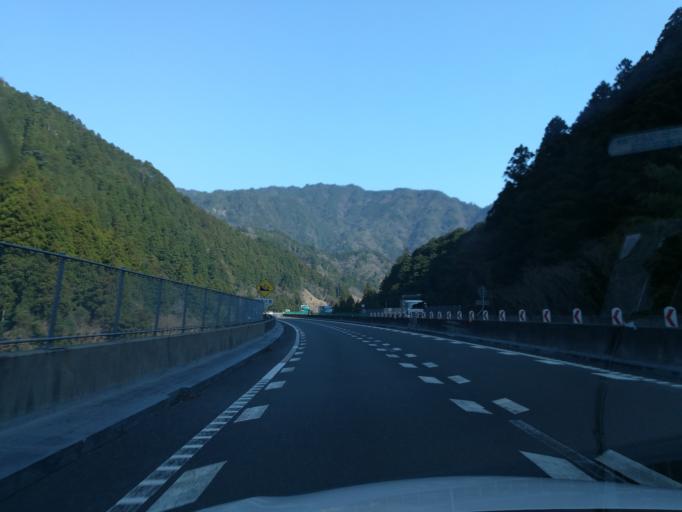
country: JP
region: Ehime
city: Kawanoecho
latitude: 33.9051
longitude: 133.6310
